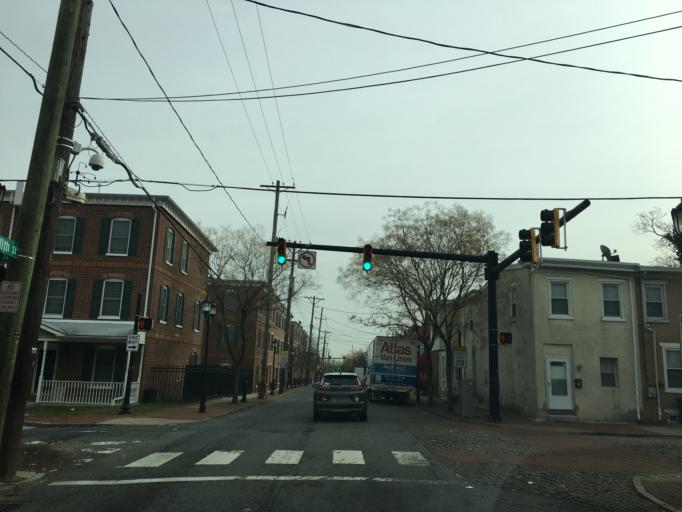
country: US
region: Delaware
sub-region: New Castle County
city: Wilmington
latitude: 39.7444
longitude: -75.5423
